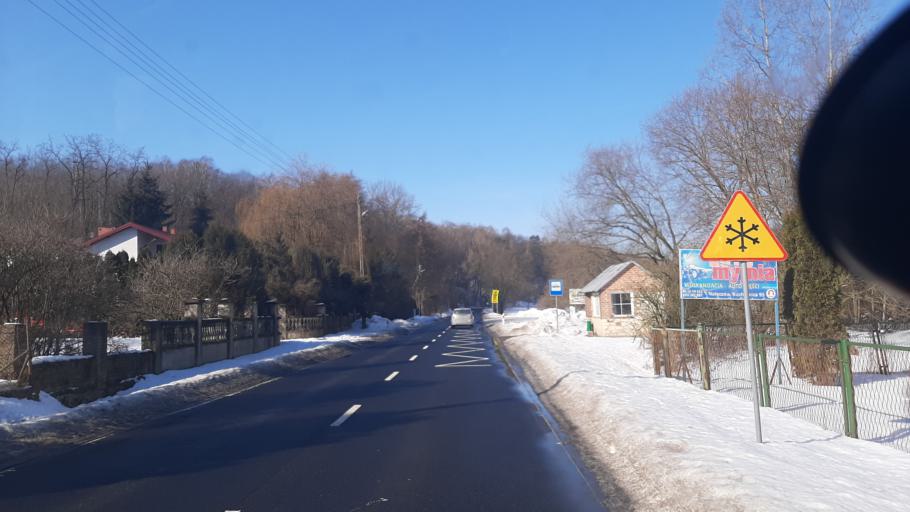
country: PL
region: Lublin Voivodeship
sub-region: Powiat pulawski
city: Wawolnica
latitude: 51.2840
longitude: 22.1695
